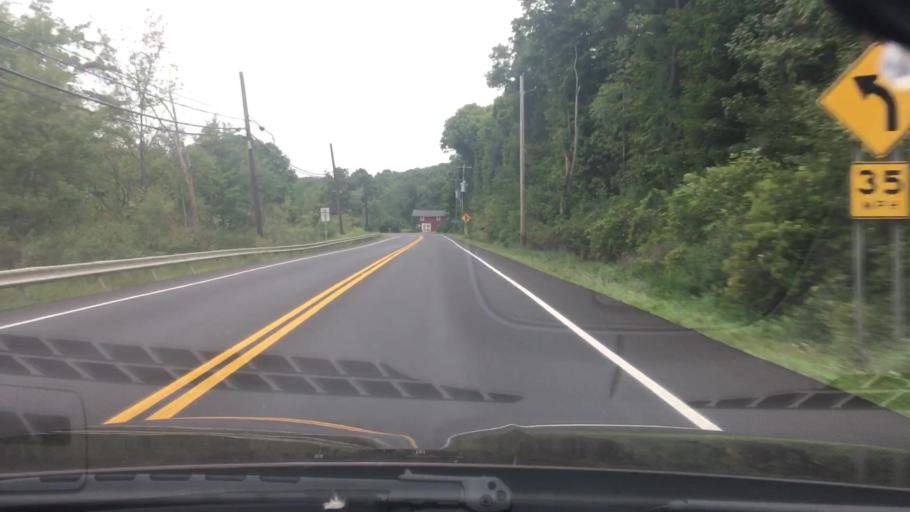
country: US
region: New York
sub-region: Dutchess County
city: Dover Plains
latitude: 41.8444
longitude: -73.5776
